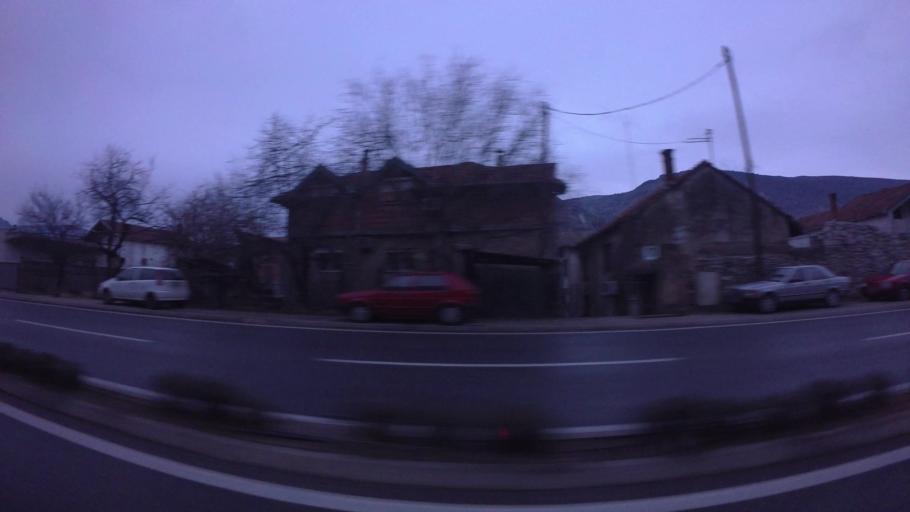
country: BA
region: Federation of Bosnia and Herzegovina
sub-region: Hercegovacko-Bosanski Kanton
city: Mostar
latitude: 43.3352
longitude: 17.8130
